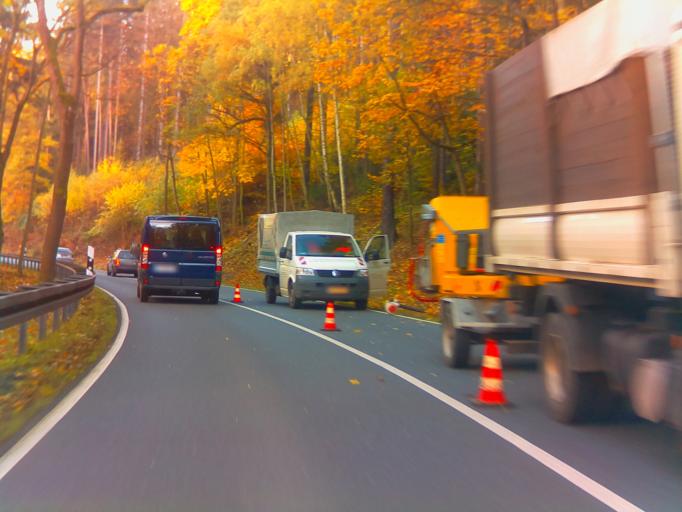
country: DE
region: Thuringia
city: Saalfeld
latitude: 50.6323
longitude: 11.3339
